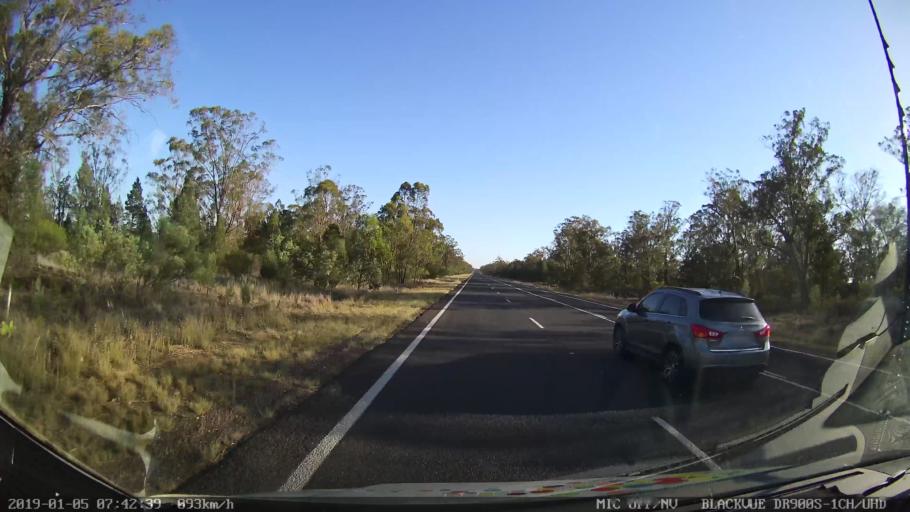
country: AU
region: New South Wales
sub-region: Gilgandra
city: Gilgandra
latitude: -31.8950
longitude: 148.6285
